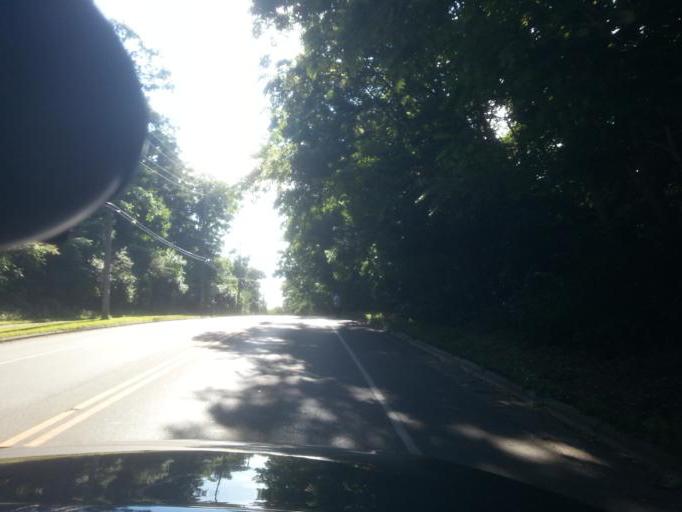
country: US
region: Wisconsin
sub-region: Dane County
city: Middleton
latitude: 43.0753
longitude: -89.4863
